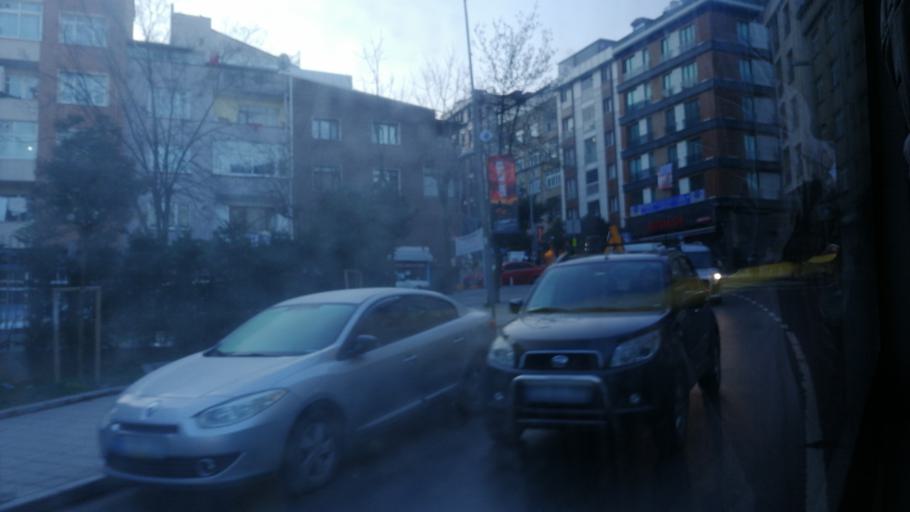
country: TR
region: Istanbul
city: Sisli
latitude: 41.0834
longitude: 28.9888
